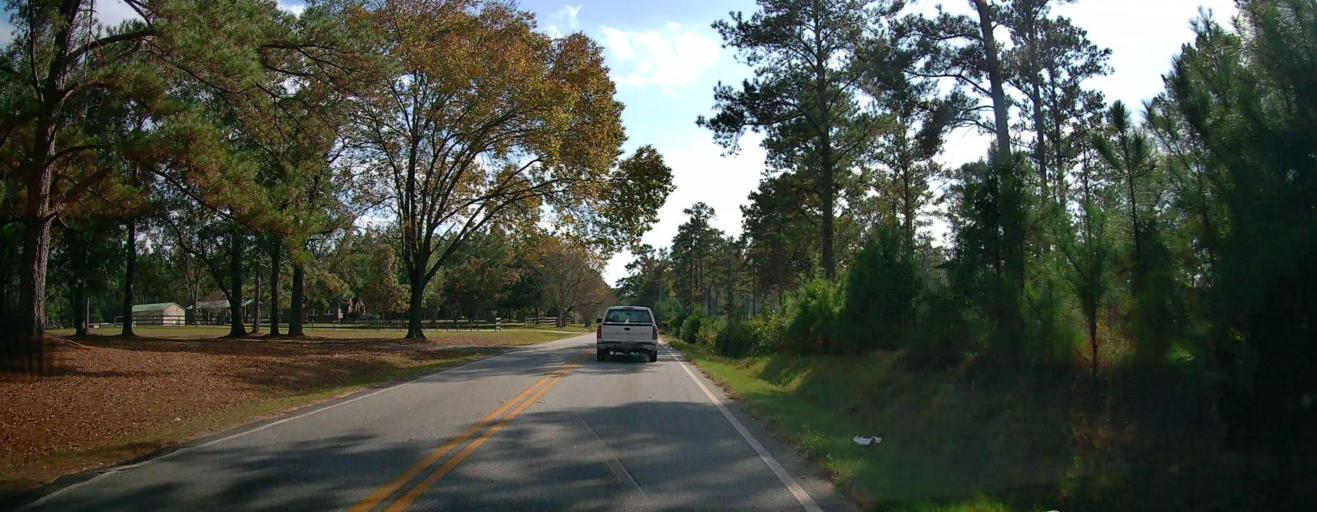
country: US
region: Georgia
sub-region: Thomas County
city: Thomasville
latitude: 30.9001
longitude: -84.0063
